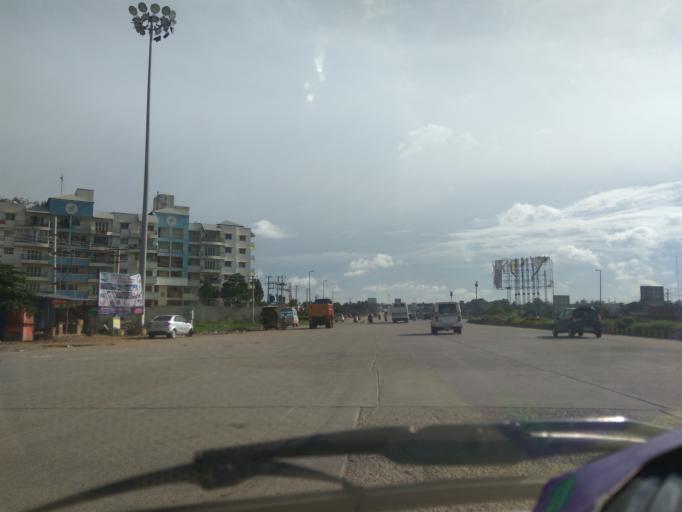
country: IN
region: Karnataka
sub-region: Bangalore Rural
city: Hoskote
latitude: 13.0606
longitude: 77.7716
